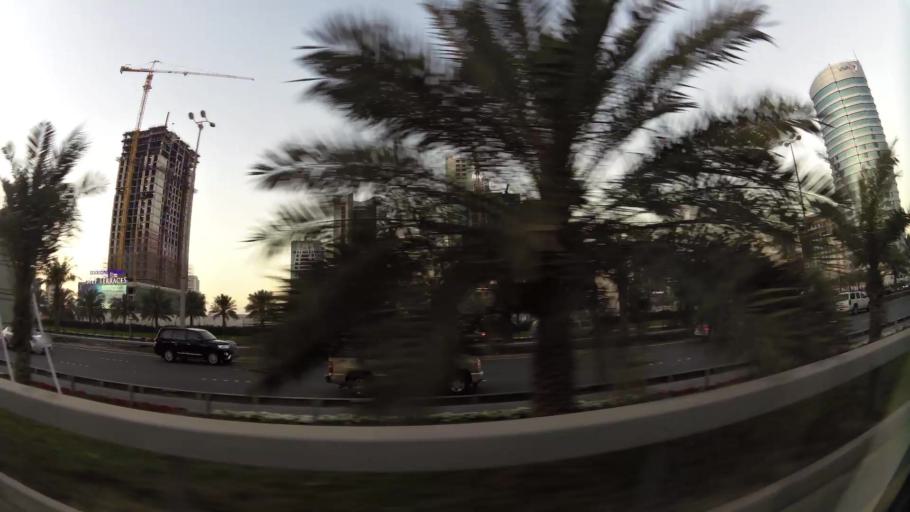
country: BH
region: Manama
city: Jidd Hafs
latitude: 26.2314
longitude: 50.5491
